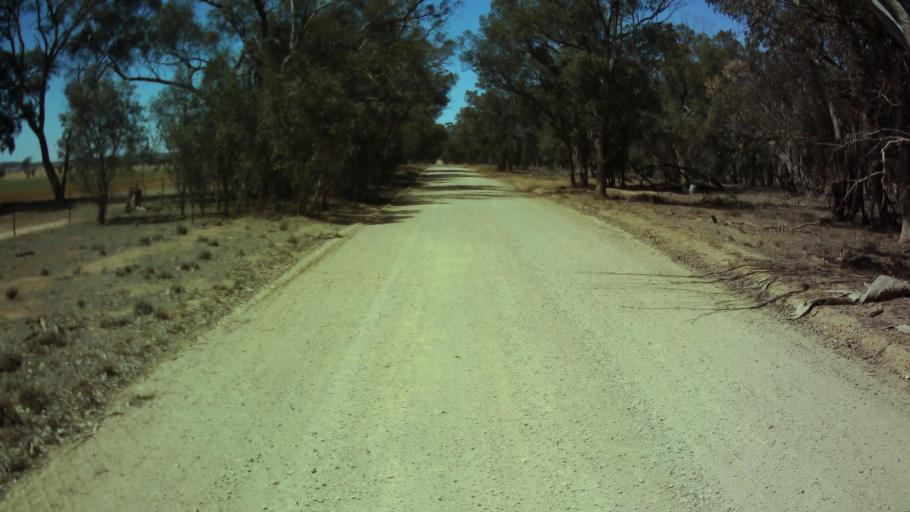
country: AU
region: New South Wales
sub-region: Weddin
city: Grenfell
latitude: -33.8808
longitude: 148.0885
